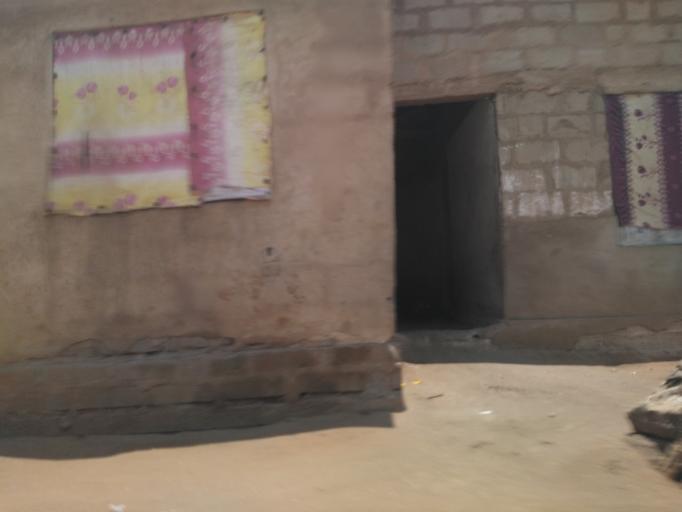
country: TZ
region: Dar es Salaam
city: Dar es Salaam
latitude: -6.8375
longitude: 39.3213
